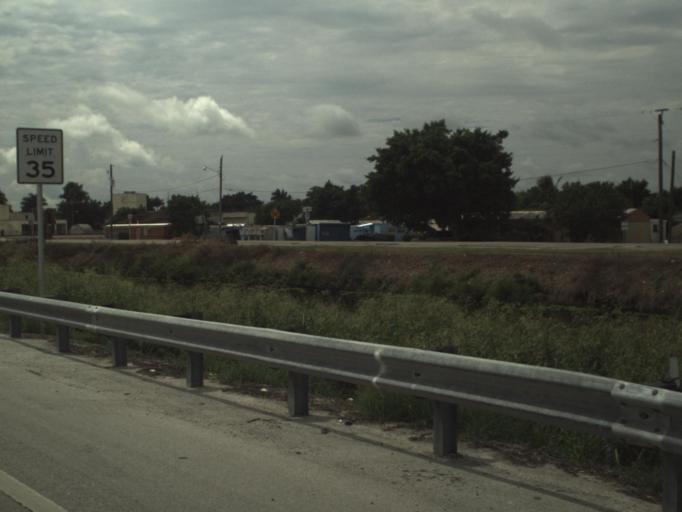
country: US
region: Florida
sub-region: Palm Beach County
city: Belle Glade
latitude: 26.6923
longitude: -80.6800
